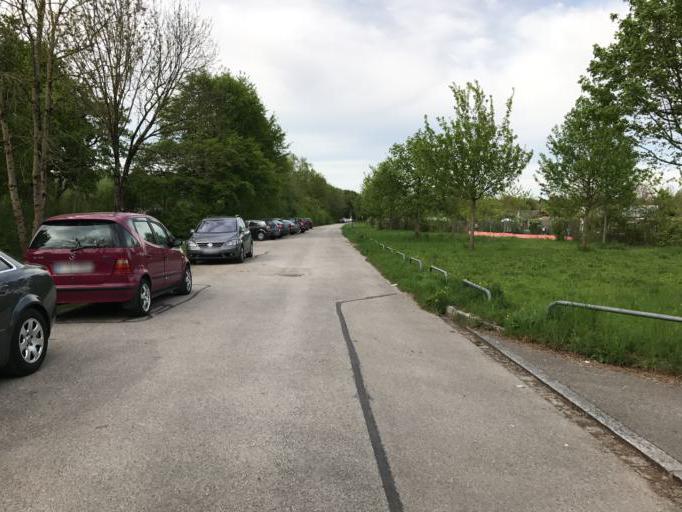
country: DE
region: Bavaria
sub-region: Upper Bavaria
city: Aschheim
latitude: 48.1347
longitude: 11.6761
